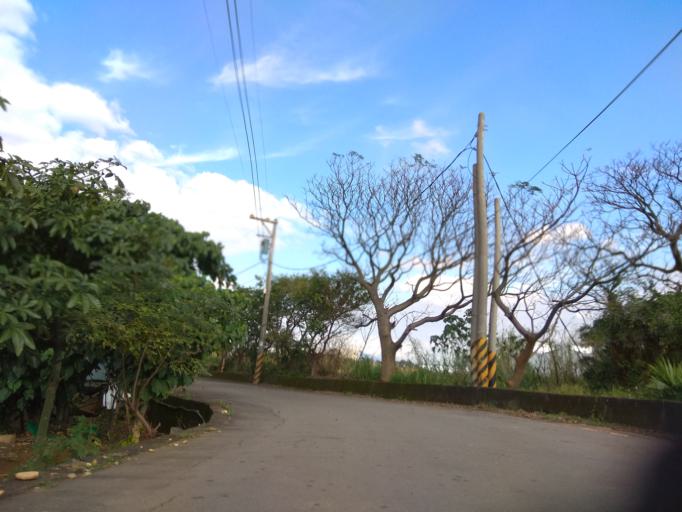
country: TW
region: Taiwan
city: Taoyuan City
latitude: 25.0506
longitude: 121.1770
